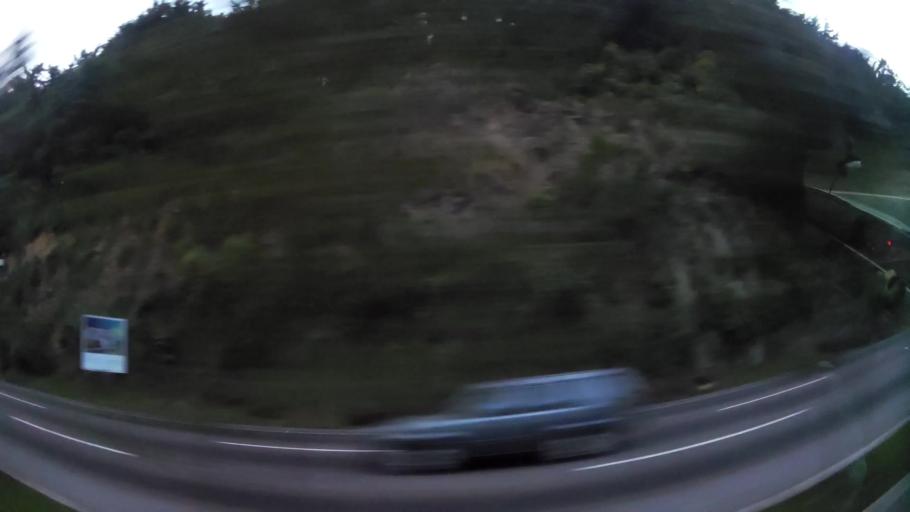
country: GT
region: Sacatepequez
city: San Lucas Sacatepequez
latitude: 14.6034
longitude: -90.6347
